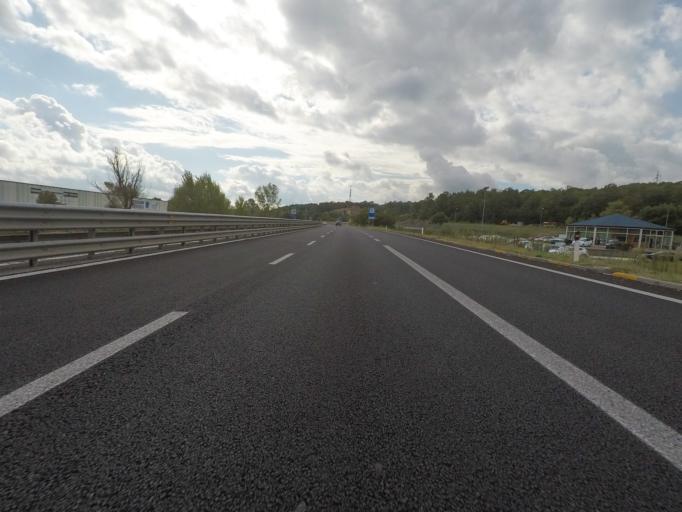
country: IT
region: Tuscany
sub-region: Provincia di Siena
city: Serre di Rapolano
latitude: 43.2669
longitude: 11.6290
